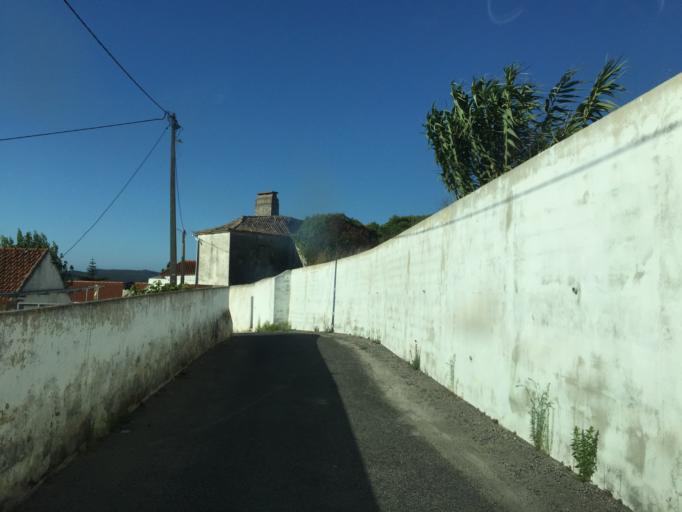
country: PT
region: Lisbon
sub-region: Torres Vedras
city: Torres Vedras
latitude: 39.0896
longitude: -9.2792
